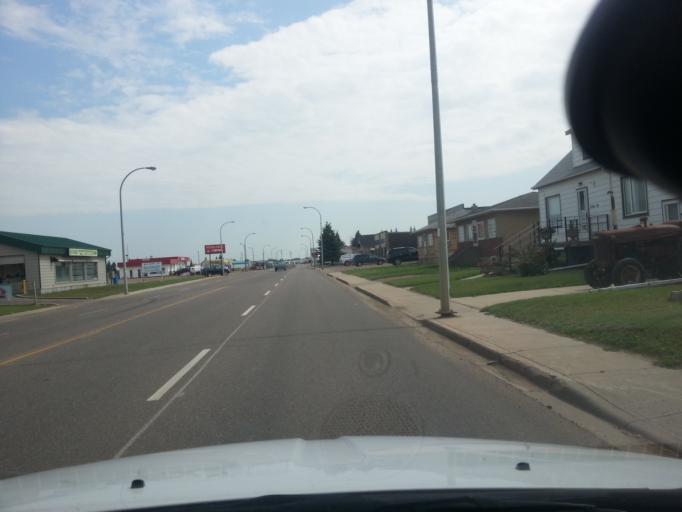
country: CA
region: Alberta
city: Vegreville
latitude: 53.4925
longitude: -112.0475
